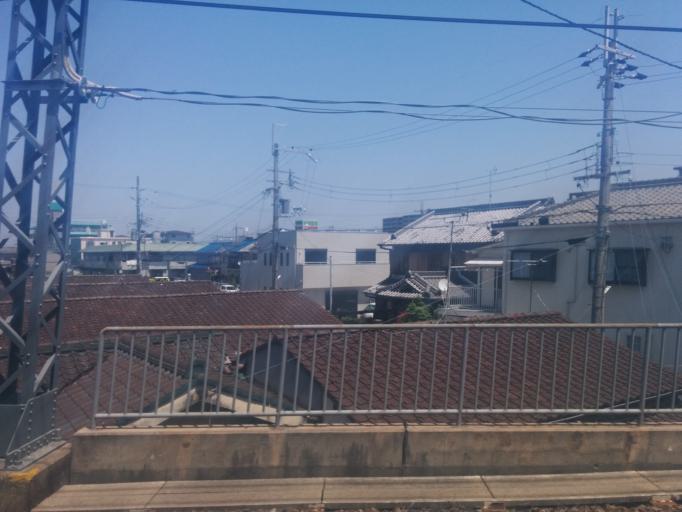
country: JP
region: Nara
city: Kashihara-shi
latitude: 34.5141
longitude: 135.7897
